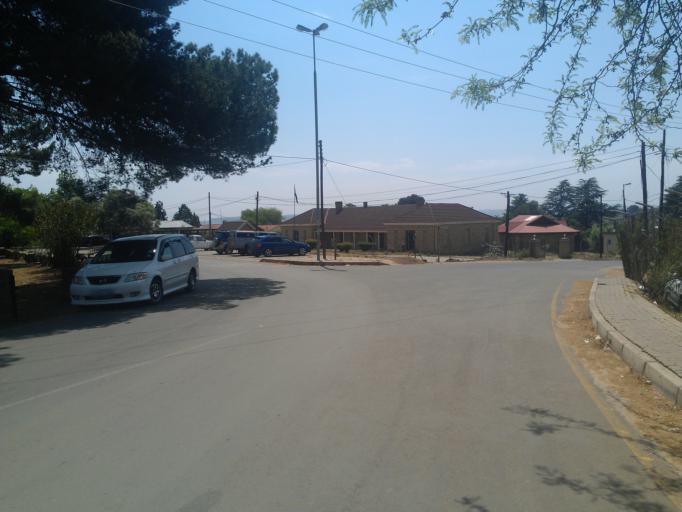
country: LS
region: Berea
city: Teyateyaneng
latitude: -29.1456
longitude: 27.7405
